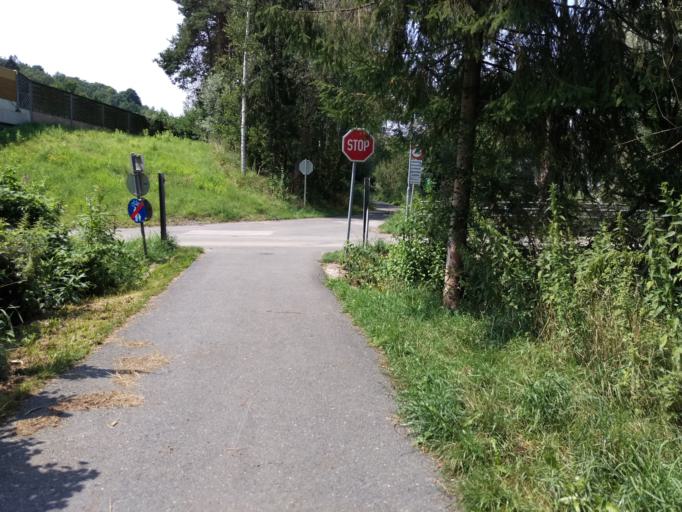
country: AT
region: Styria
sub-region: Politischer Bezirk Graz-Umgebung
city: Hart bei Graz
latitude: 47.0429
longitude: 15.5229
